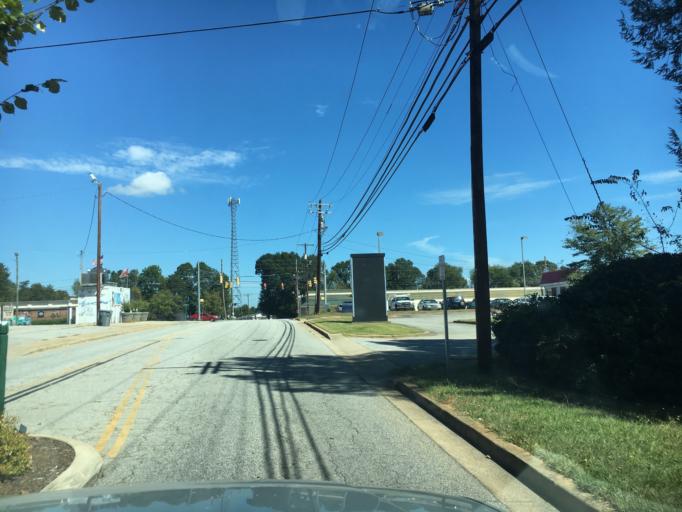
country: US
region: South Carolina
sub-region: Spartanburg County
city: Spartanburg
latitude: 34.9322
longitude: -81.8991
